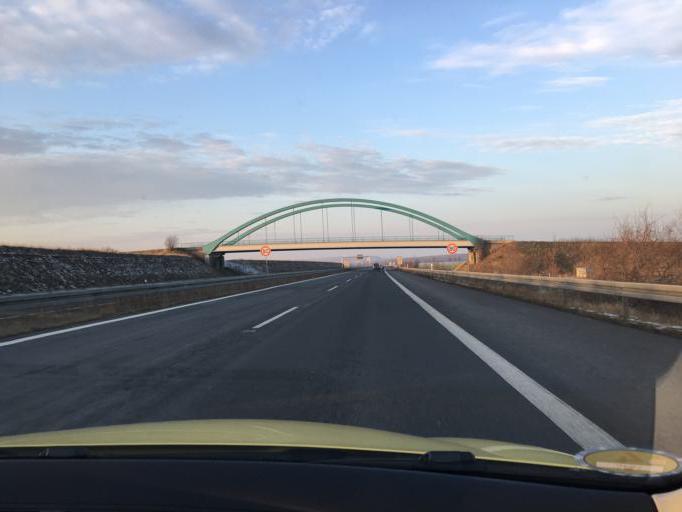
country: DE
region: Saxony
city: Borna
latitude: 51.1212
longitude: 12.5182
